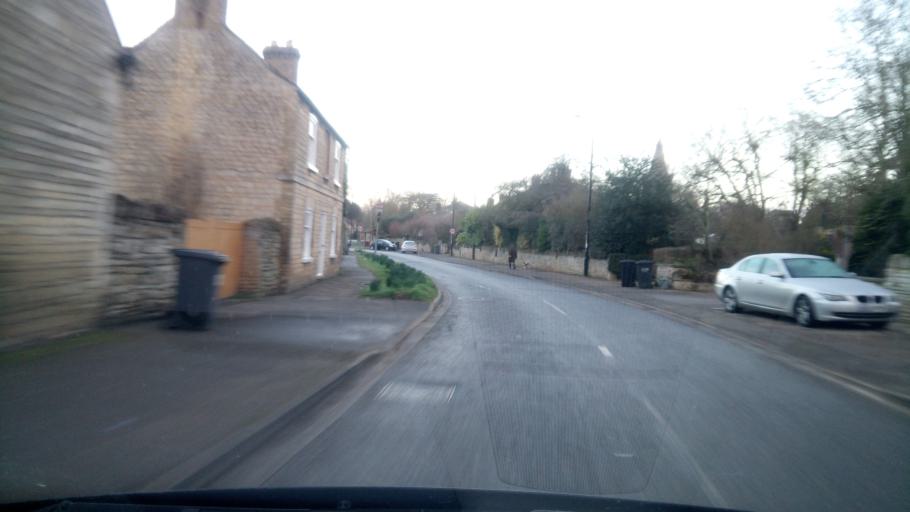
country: GB
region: England
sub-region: Peterborough
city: Castor
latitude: 52.5708
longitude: -0.3409
